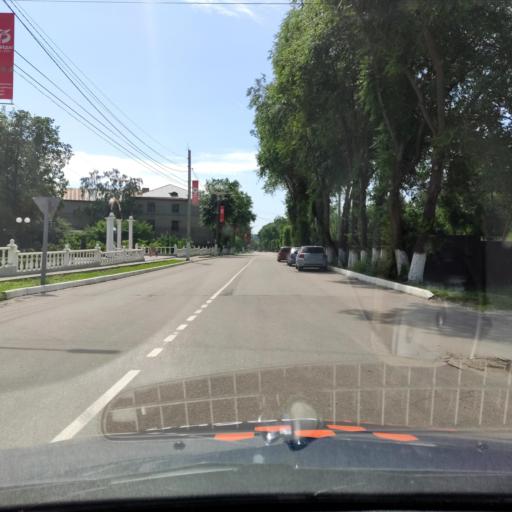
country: RU
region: Voronezj
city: Semiluki
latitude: 51.6870
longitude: 39.0393
